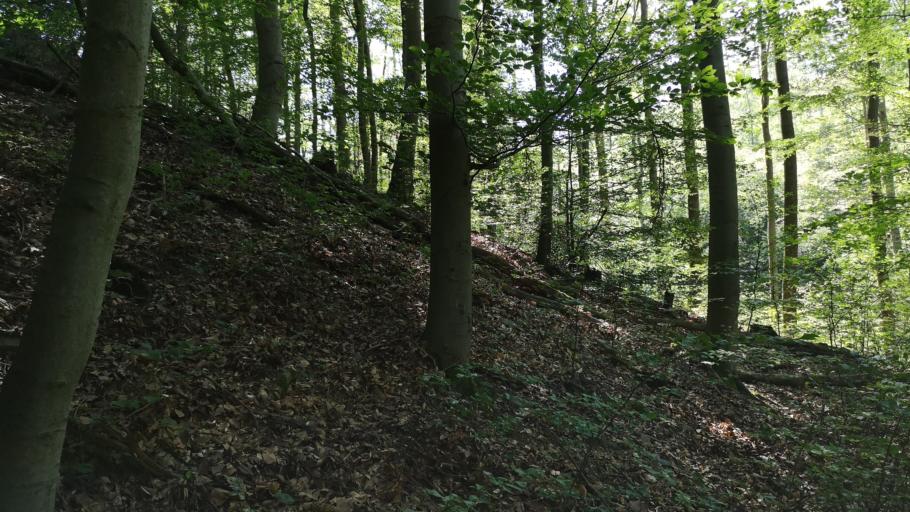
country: DE
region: Saxony-Anhalt
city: Stolberg
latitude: 51.5579
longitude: 10.9638
